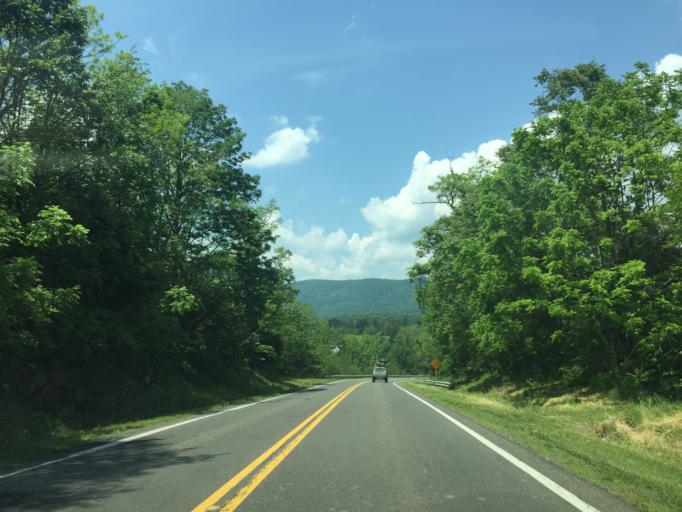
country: US
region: Virginia
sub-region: Shenandoah County
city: Strasburg
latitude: 39.0336
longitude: -78.3790
